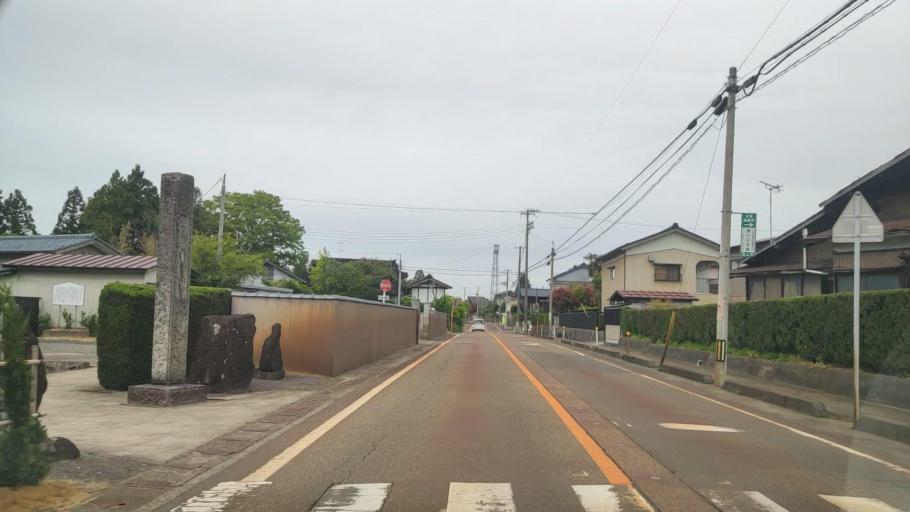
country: JP
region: Niigata
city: Shirone
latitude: 37.7249
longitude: 139.0793
